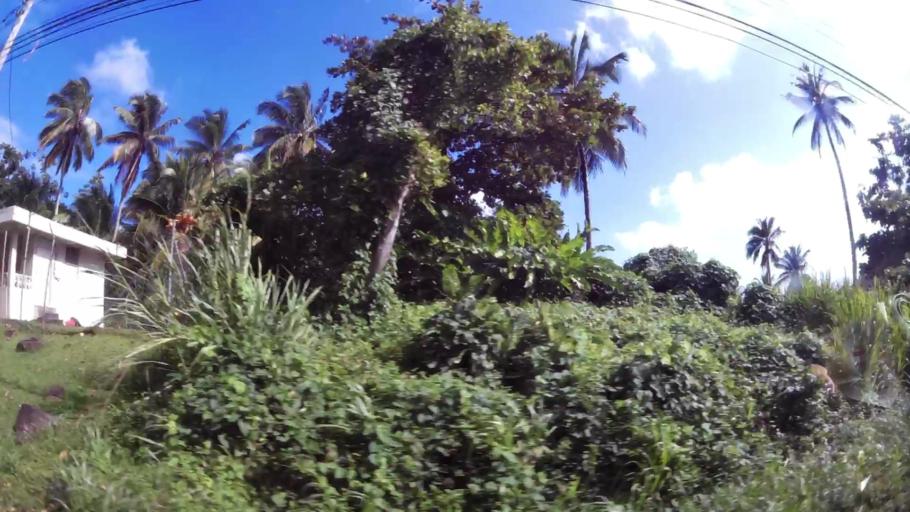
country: DM
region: Saint David
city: Castle Bruce
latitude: 15.4761
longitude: -61.2516
